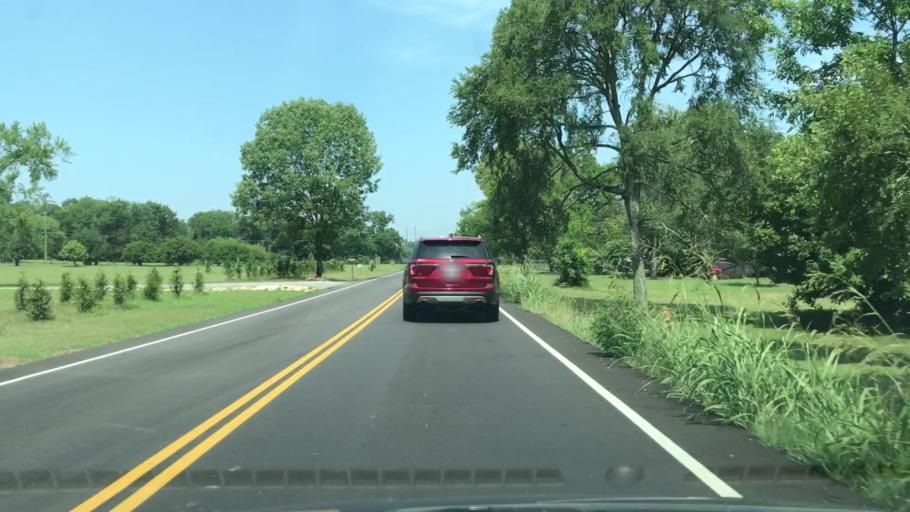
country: US
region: Tennessee
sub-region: Wilson County
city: Rural Hill
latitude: 36.1195
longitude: -86.4974
